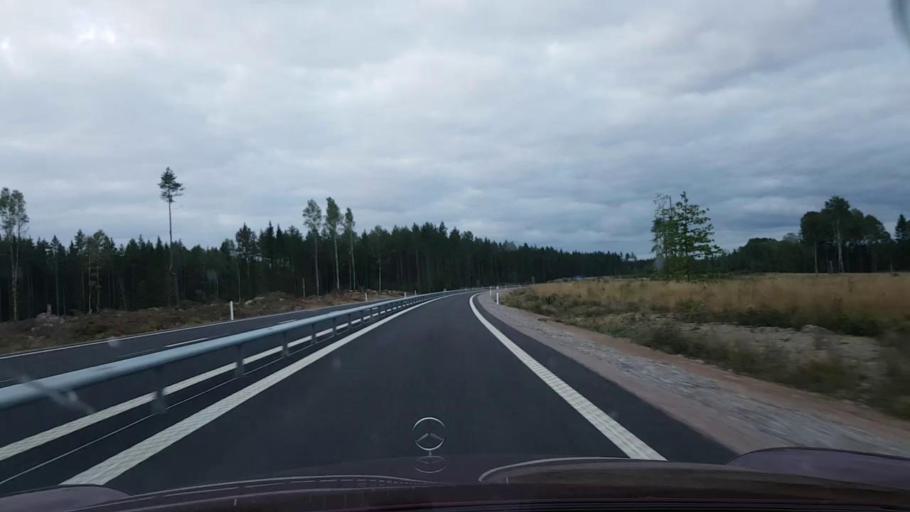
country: SE
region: Vaestmanland
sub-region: Hallstahammars Kommun
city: Hallstahammar
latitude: 59.6541
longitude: 16.2040
